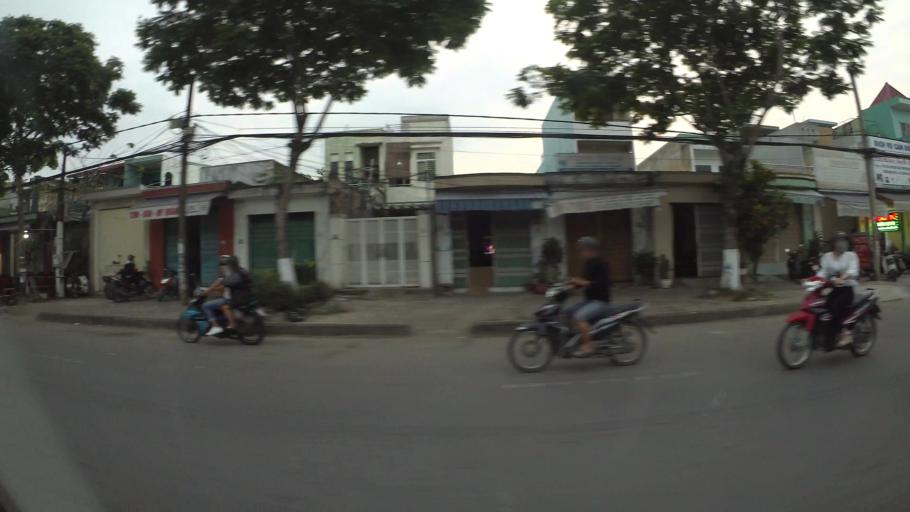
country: VN
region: Da Nang
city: Lien Chieu
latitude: 16.0802
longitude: 108.1469
